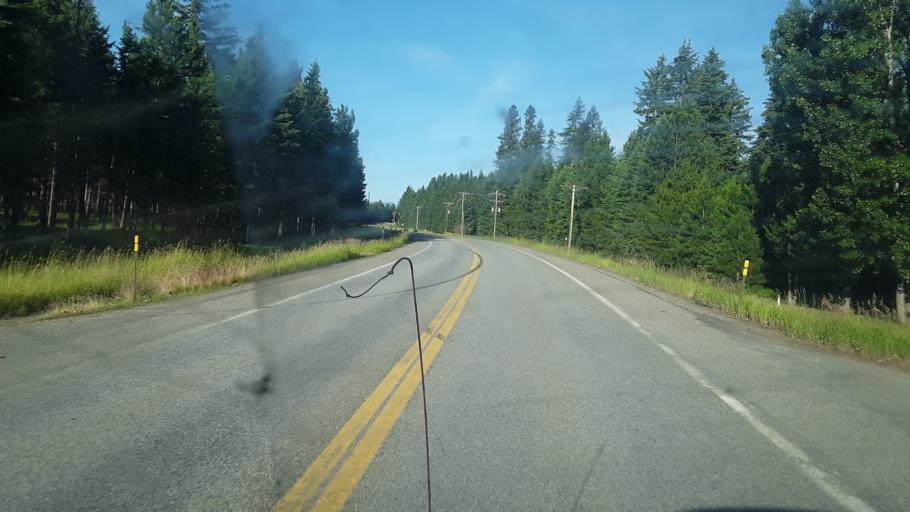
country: US
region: Idaho
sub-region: Boundary County
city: Bonners Ferry
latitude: 48.7321
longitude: -116.1901
